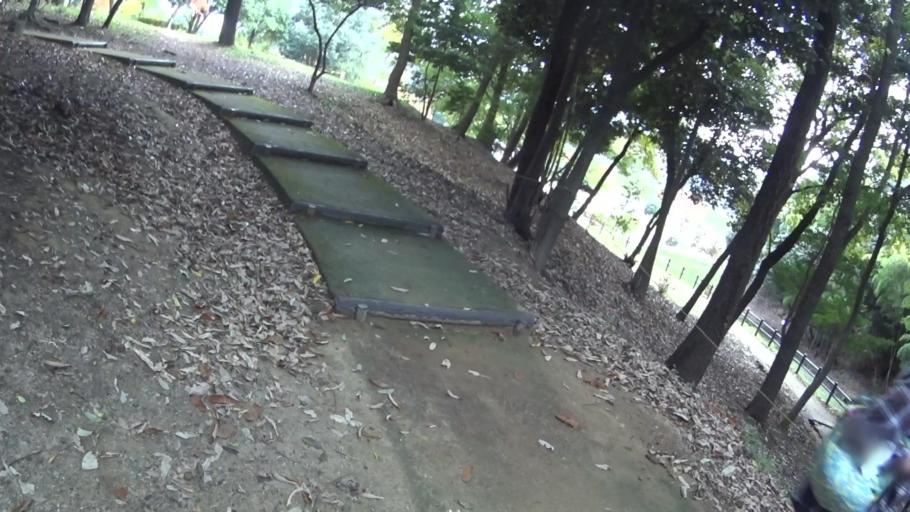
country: JP
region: Osaka
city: Kashihara
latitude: 34.5518
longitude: 135.5946
